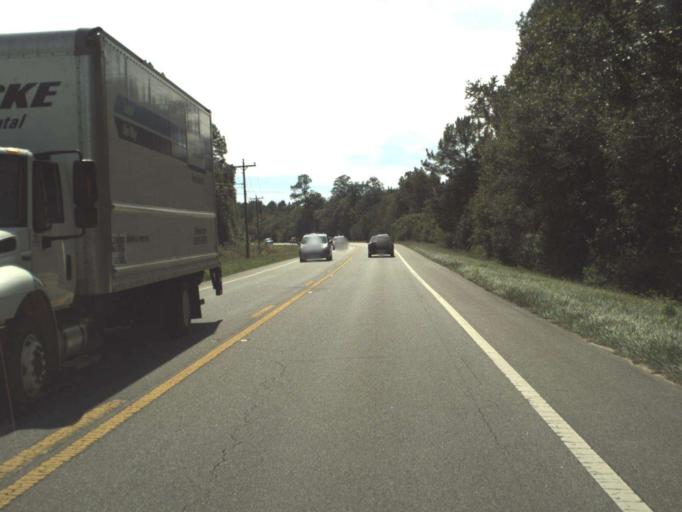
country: US
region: Florida
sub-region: Washington County
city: Chipley
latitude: 30.6440
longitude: -85.5846
